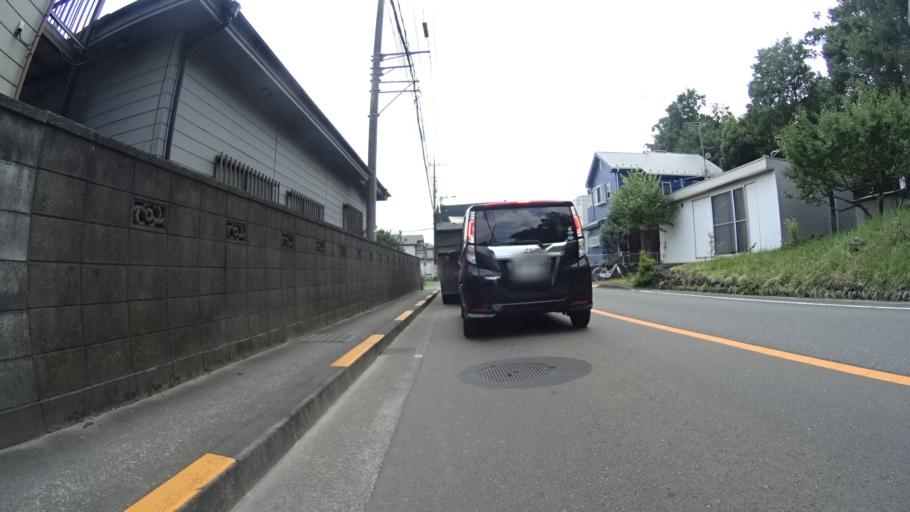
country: JP
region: Tokyo
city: Fussa
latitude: 35.7452
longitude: 139.3195
